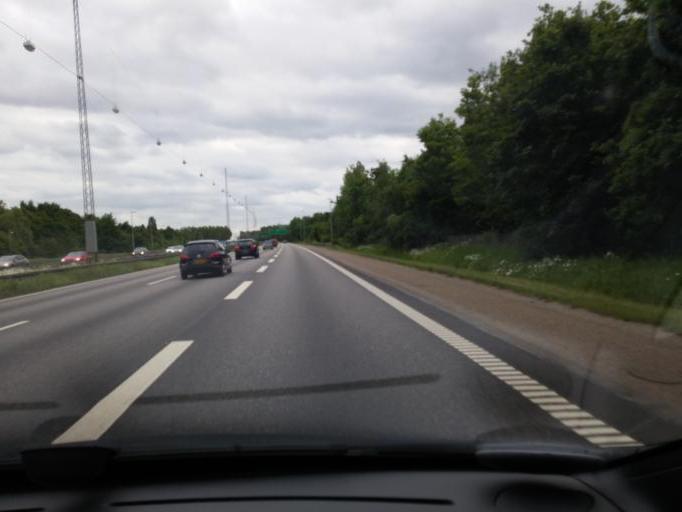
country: DK
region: Capital Region
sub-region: Brondby Kommune
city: Brondbyvester
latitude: 55.6497
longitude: 12.4230
